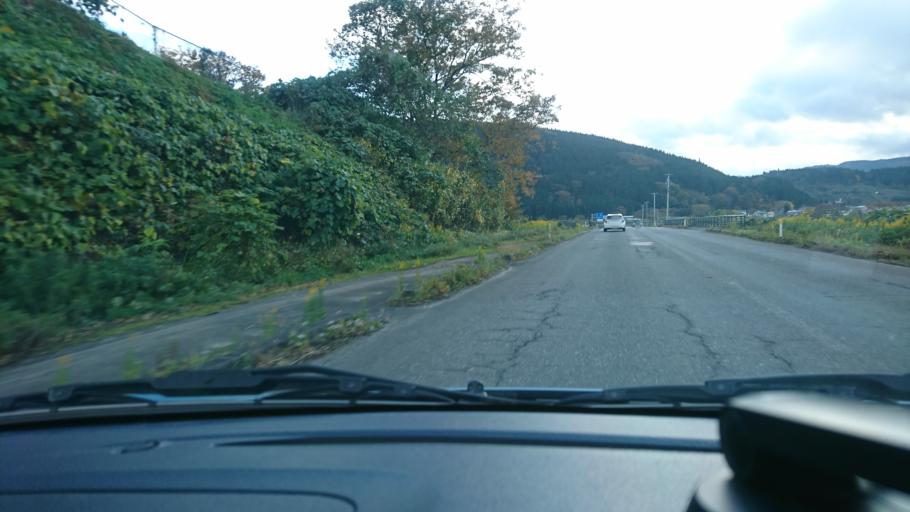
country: JP
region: Miyagi
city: Furukawa
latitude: 38.7360
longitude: 140.7746
